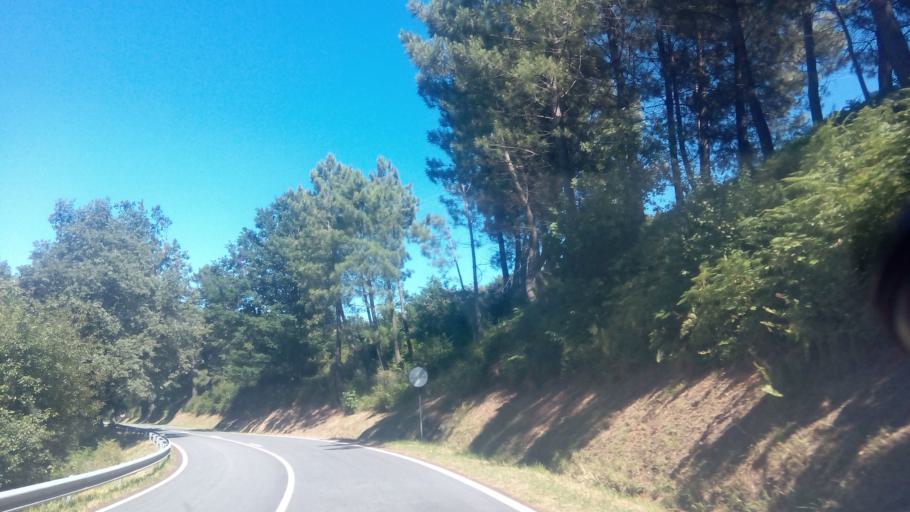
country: PT
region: Vila Real
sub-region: Santa Marta de Penaguiao
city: Santa Marta de Penaguiao
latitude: 41.2793
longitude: -7.8533
